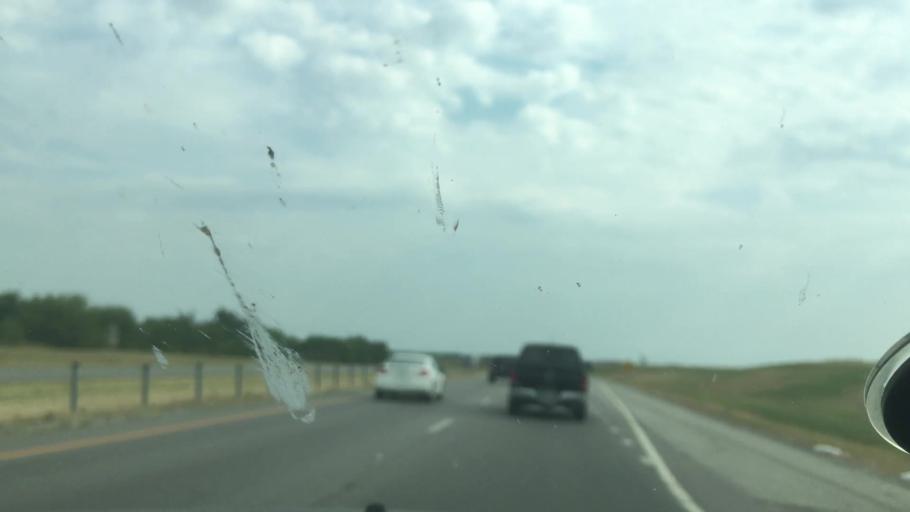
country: US
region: Oklahoma
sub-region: Bryan County
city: Calera
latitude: 33.9624
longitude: -96.4165
